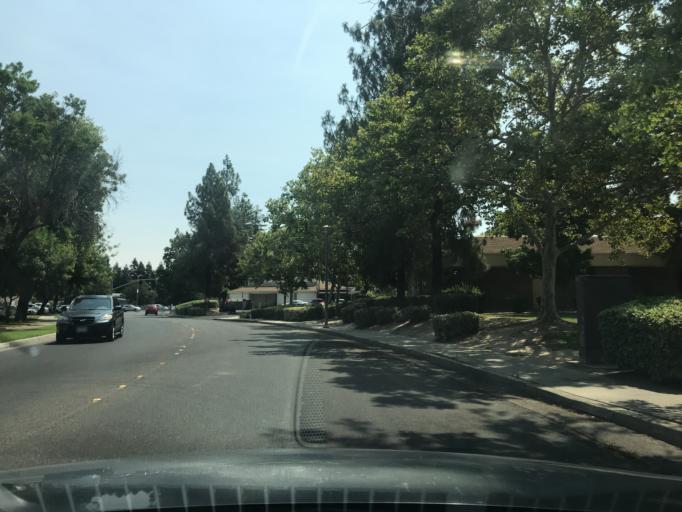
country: US
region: California
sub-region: Merced County
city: Merced
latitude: 37.3150
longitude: -120.4712
